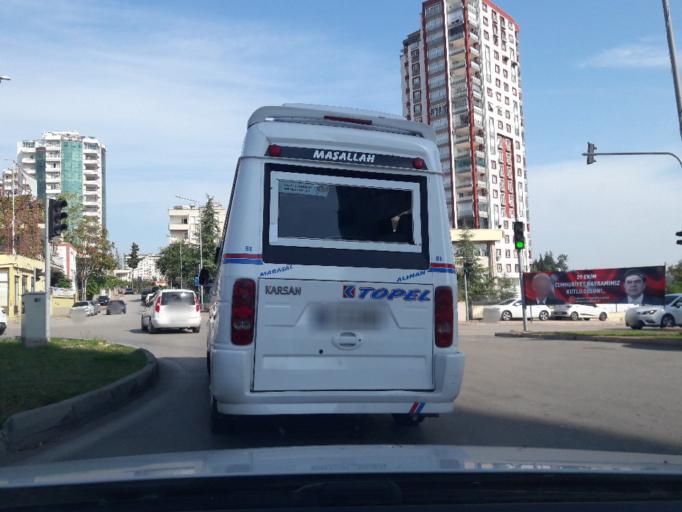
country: TR
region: Adana
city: Adana
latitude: 37.0221
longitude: 35.3195
